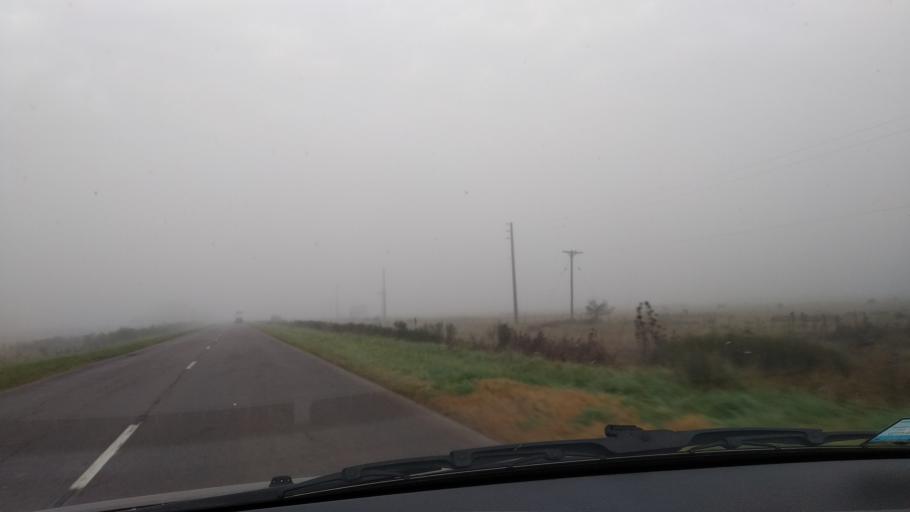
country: AR
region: Buenos Aires
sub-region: Partido de San Vicente
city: San Vicente
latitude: -35.2644
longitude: -58.5227
